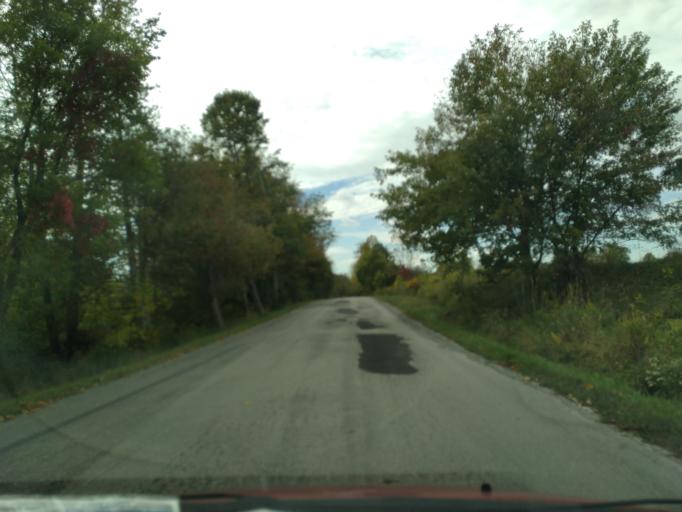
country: CA
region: Ontario
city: Keswick
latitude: 44.2611
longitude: -79.3474
